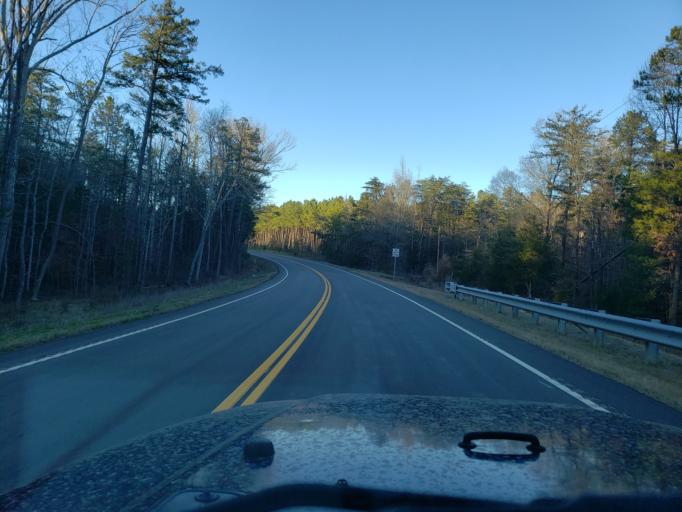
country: US
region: South Carolina
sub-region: Cherokee County
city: Blacksburg
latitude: 35.0365
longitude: -81.4037
